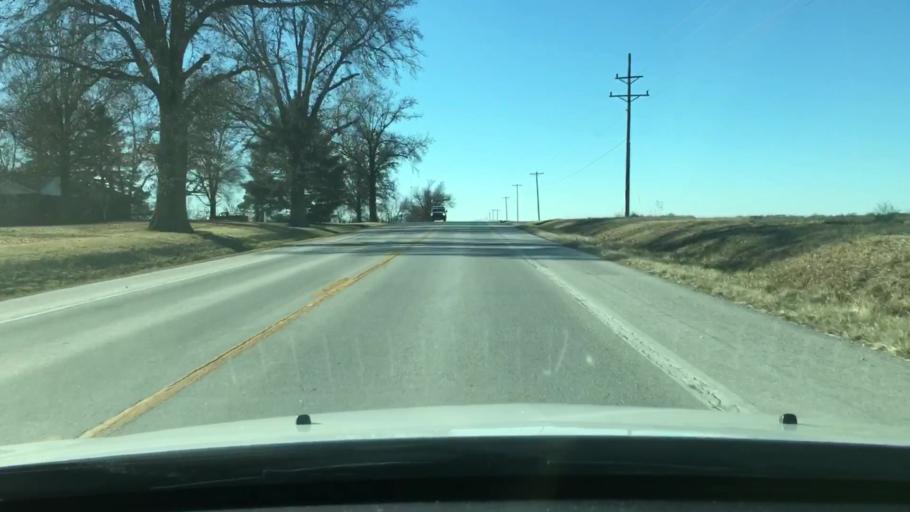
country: US
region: Missouri
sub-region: Pike County
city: Bowling Green
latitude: 39.3445
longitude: -91.2796
